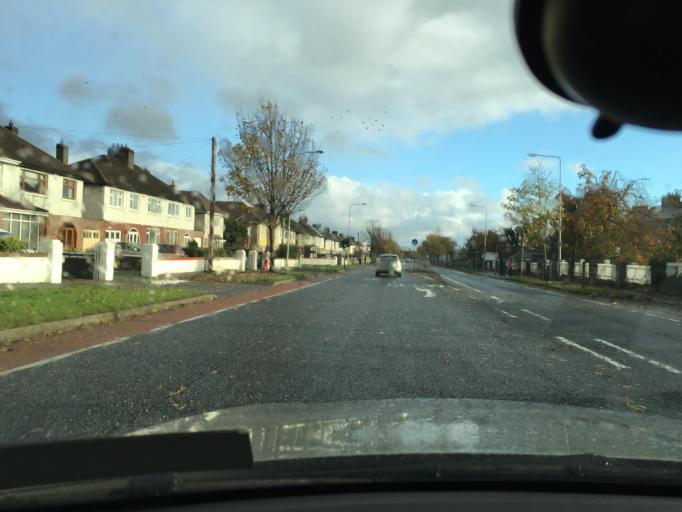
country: IE
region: Leinster
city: Chapelizod
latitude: 53.3701
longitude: -6.3256
